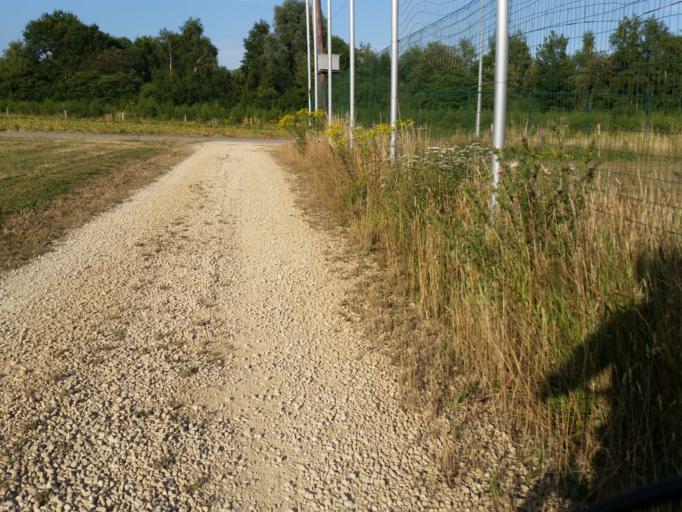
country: BE
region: Flanders
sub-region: Provincie Vlaams-Brabant
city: Zemst
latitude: 50.9797
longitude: 4.4781
